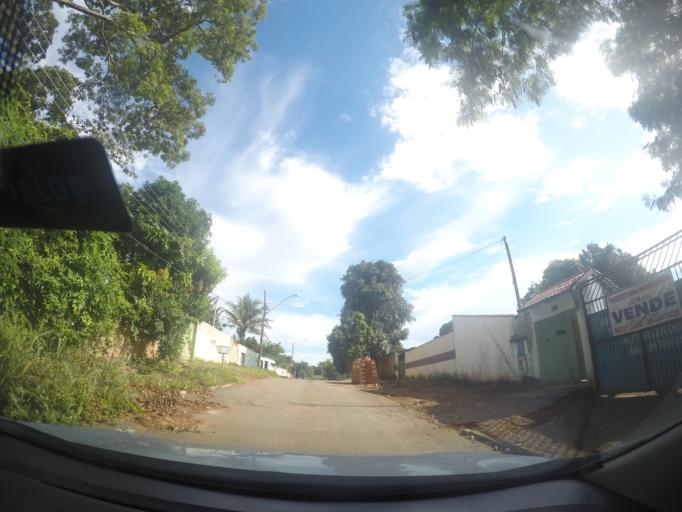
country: BR
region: Goias
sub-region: Goiania
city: Goiania
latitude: -16.6722
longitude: -49.1994
